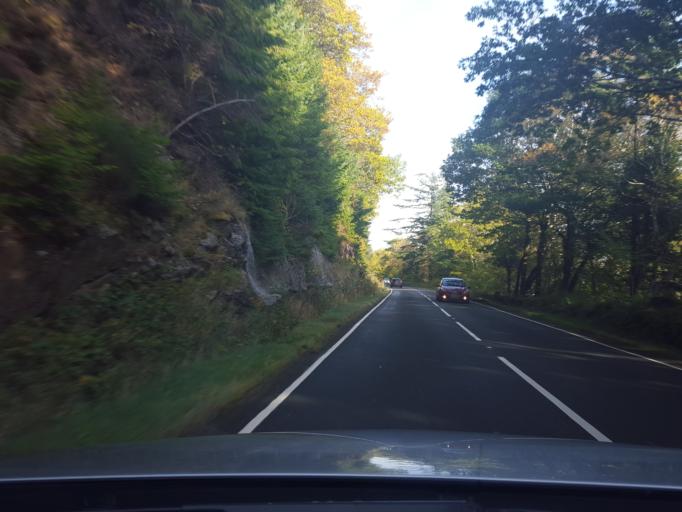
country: GB
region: Scotland
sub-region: Highland
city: Beauly
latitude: 57.2696
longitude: -4.5058
